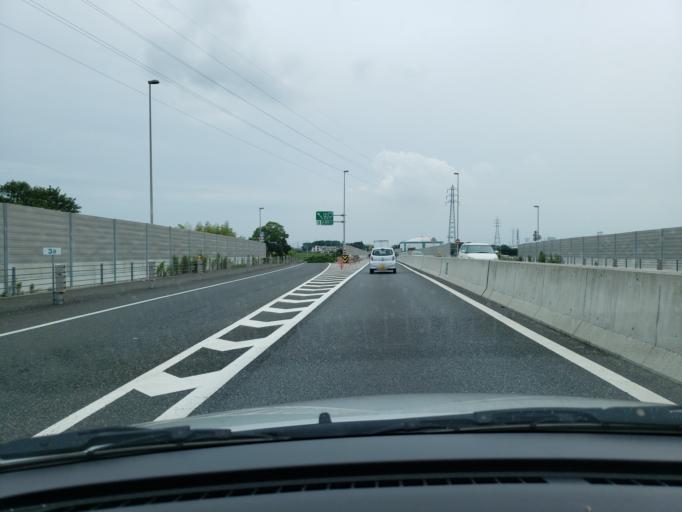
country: JP
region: Hyogo
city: Kakogawacho-honmachi
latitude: 34.7751
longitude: 134.8915
